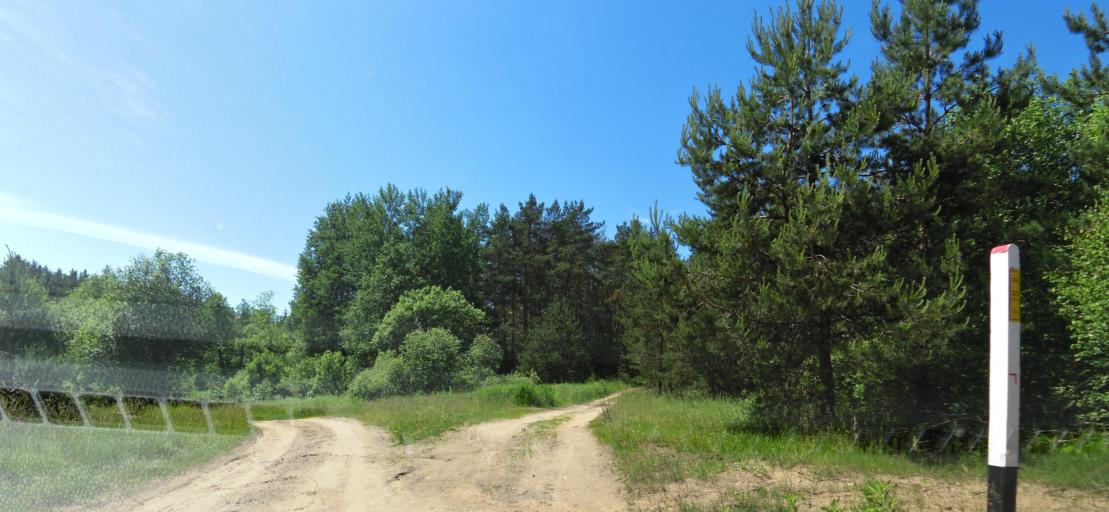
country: LT
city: Moletai
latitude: 55.0721
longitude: 25.2442
